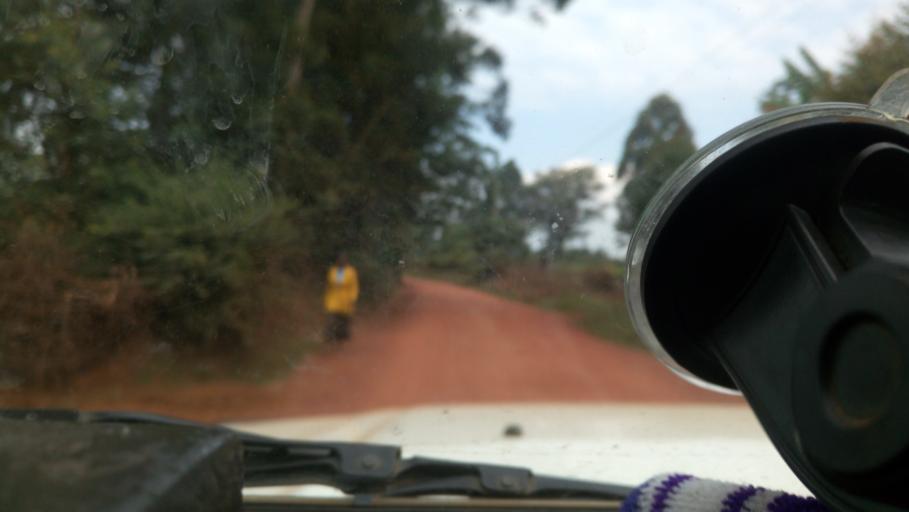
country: KE
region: Kericho
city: Litein
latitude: -0.6147
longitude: 35.2177
